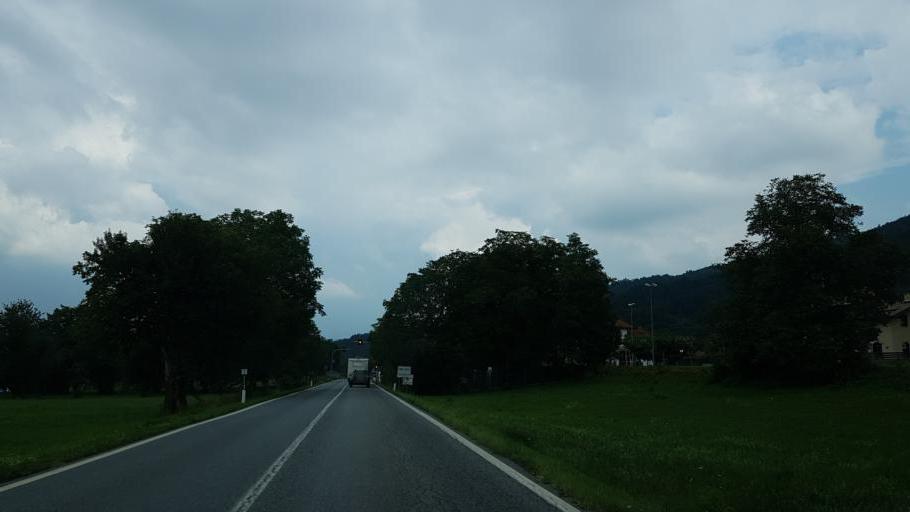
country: IT
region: Piedmont
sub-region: Provincia di Cuneo
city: Roccasparvera
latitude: 44.3349
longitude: 7.4315
